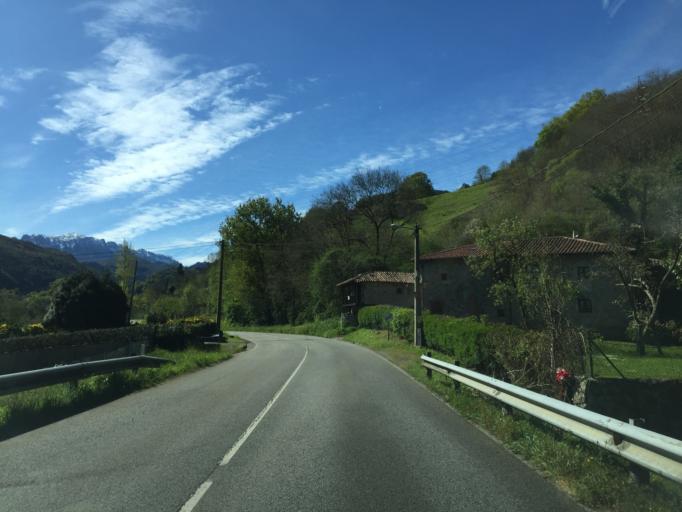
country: ES
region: Asturias
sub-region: Province of Asturias
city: Proaza
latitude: 43.3212
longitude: -5.9929
